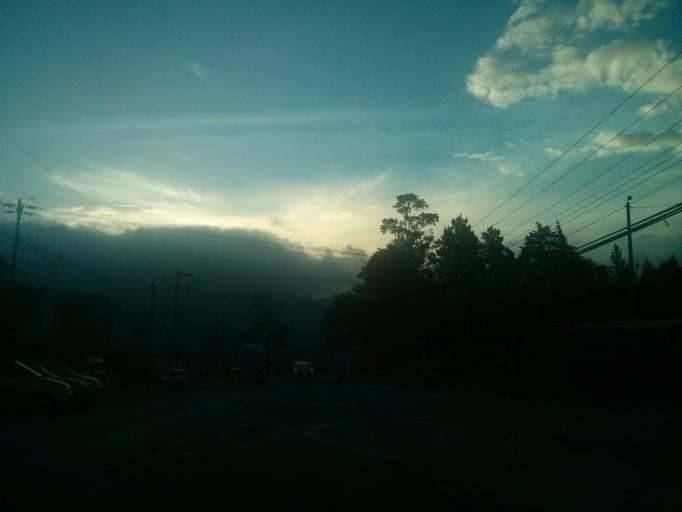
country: CR
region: Cartago
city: Cartago
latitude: 9.8784
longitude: -83.9294
